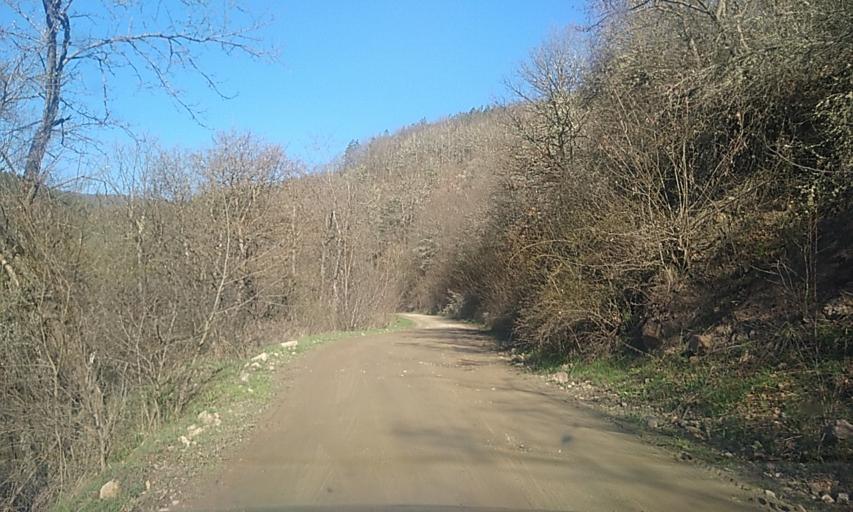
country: RS
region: Central Serbia
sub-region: Pcinjski Okrug
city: Bosilegrad
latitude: 42.3584
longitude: 22.4133
